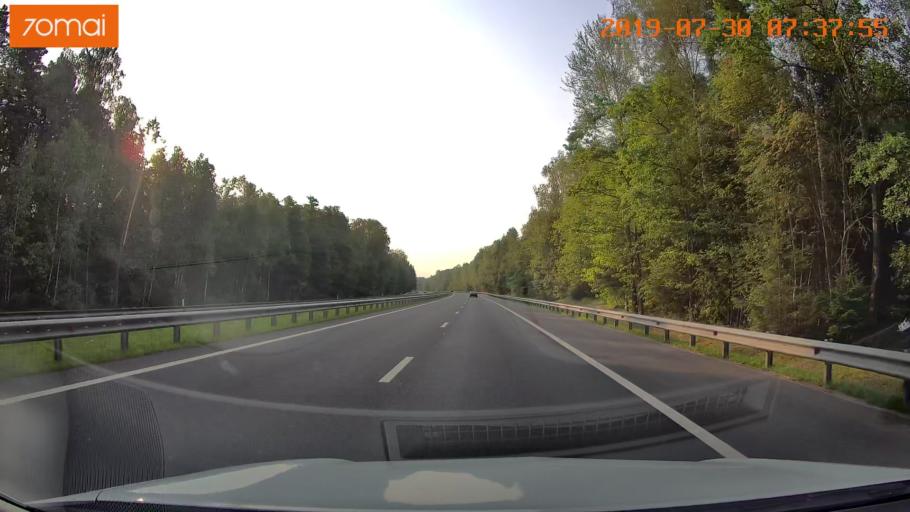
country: RU
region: Kaliningrad
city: Gvardeysk
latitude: 54.6527
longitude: 21.1549
